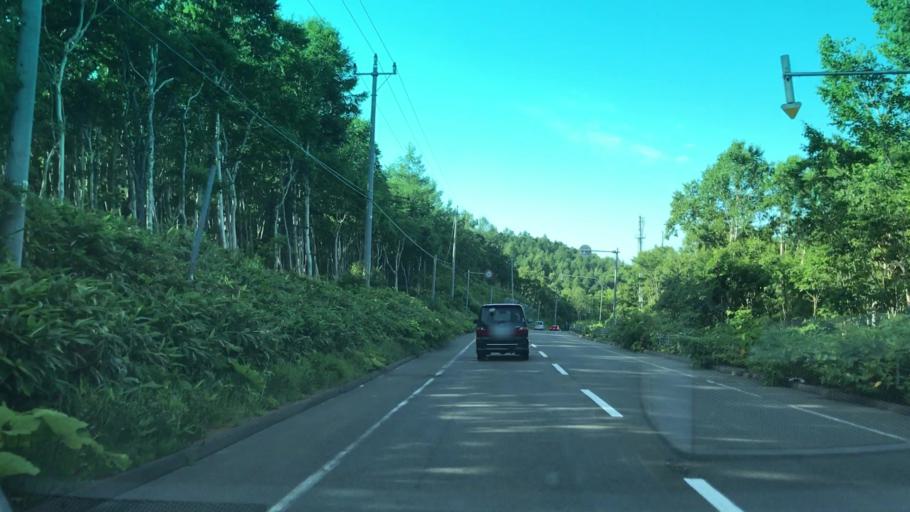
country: JP
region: Hokkaido
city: Otaru
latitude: 43.1065
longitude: 141.0048
